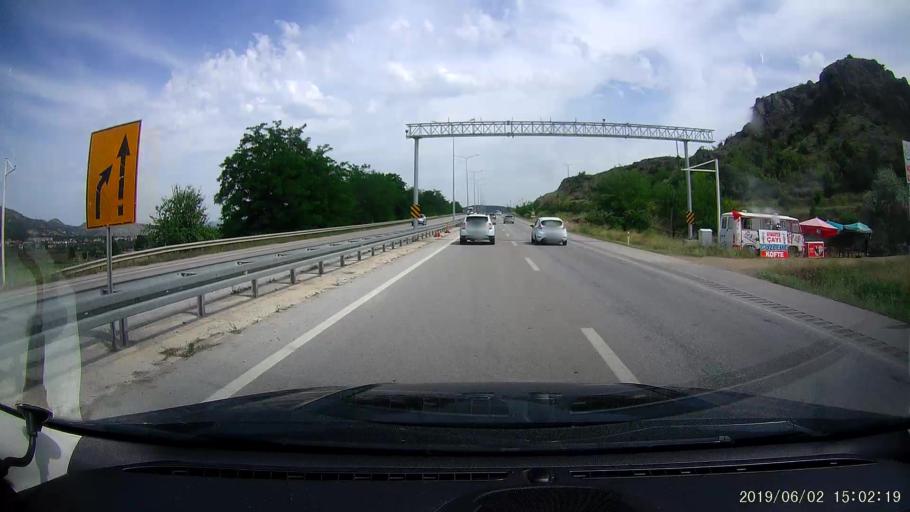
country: TR
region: Corum
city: Osmancik
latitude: 40.9820
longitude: 34.7655
